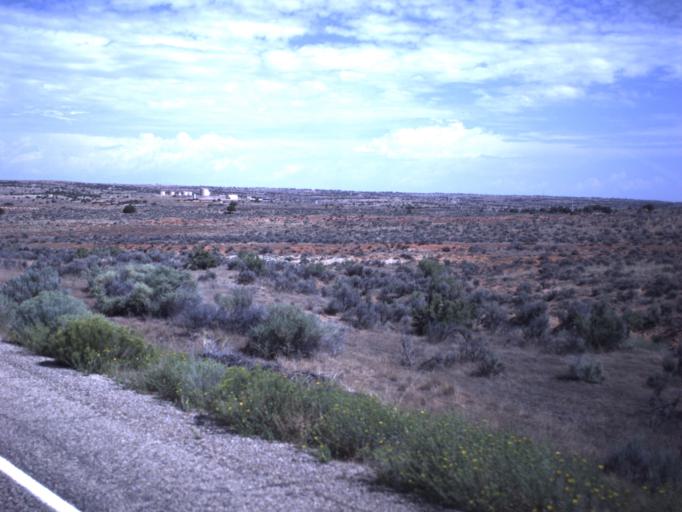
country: US
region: Utah
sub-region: Uintah County
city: Naples
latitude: 40.1597
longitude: -109.3091
